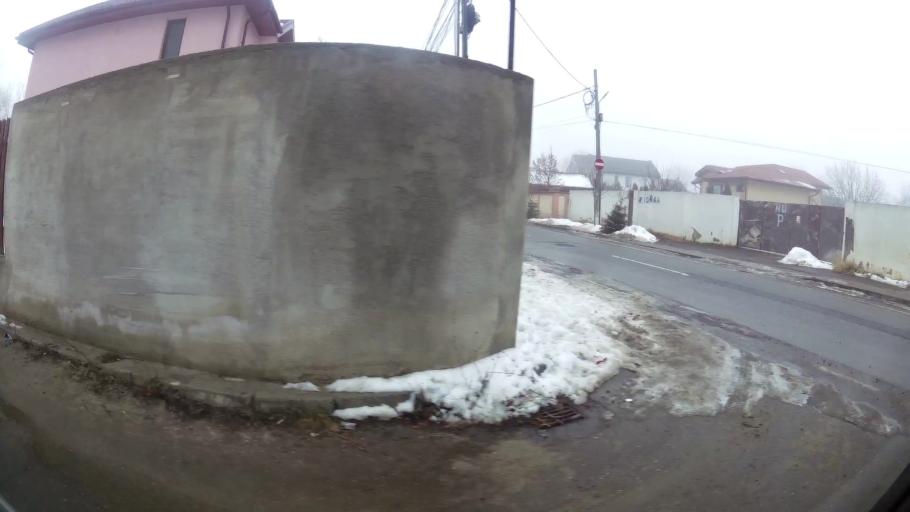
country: RO
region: Ilfov
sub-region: Comuna Chiajna
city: Chiajna
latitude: 44.4557
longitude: 25.9808
